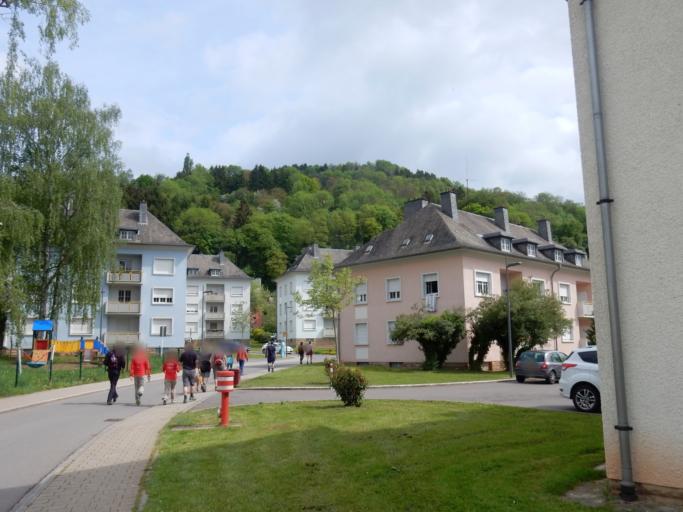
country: LU
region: Diekirch
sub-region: Canton de Diekirch
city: Diekirch
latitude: 49.8682
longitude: 6.1632
